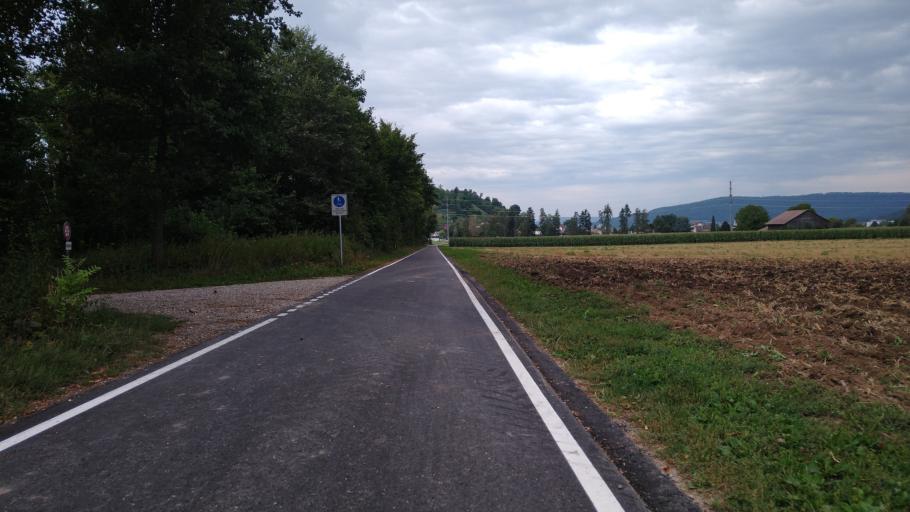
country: CH
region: Aargau
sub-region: Bezirk Lenzburg
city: Staufen
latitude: 47.3699
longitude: 8.1660
